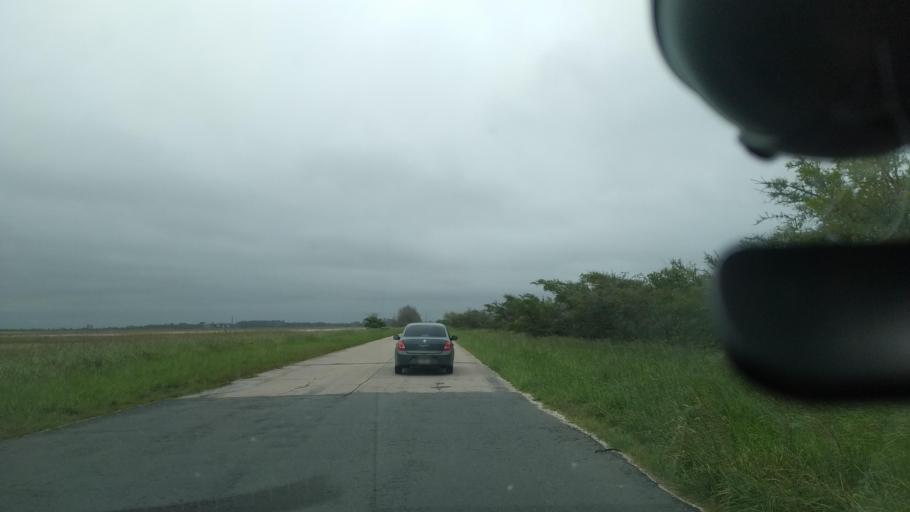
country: AR
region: Buenos Aires
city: Veronica
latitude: -35.5595
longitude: -57.3032
